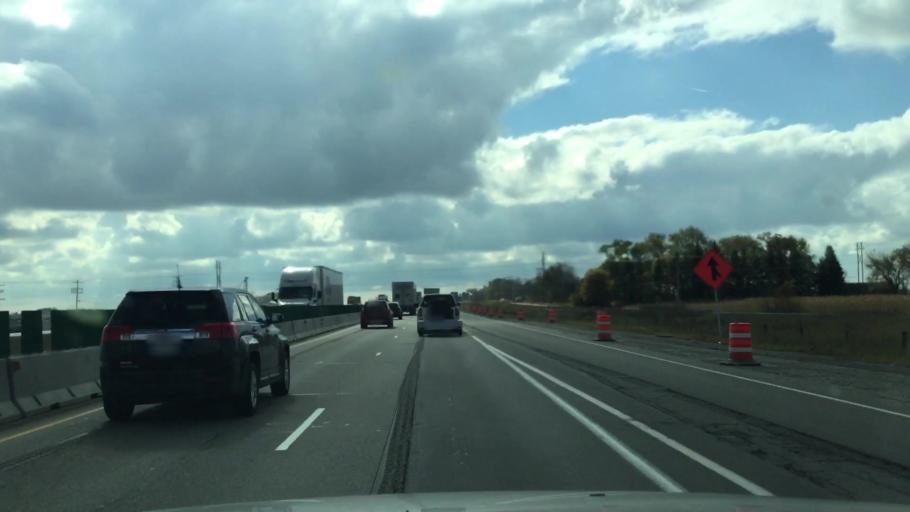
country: US
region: Wisconsin
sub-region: Kenosha County
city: Somers
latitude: 42.6365
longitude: -87.9528
